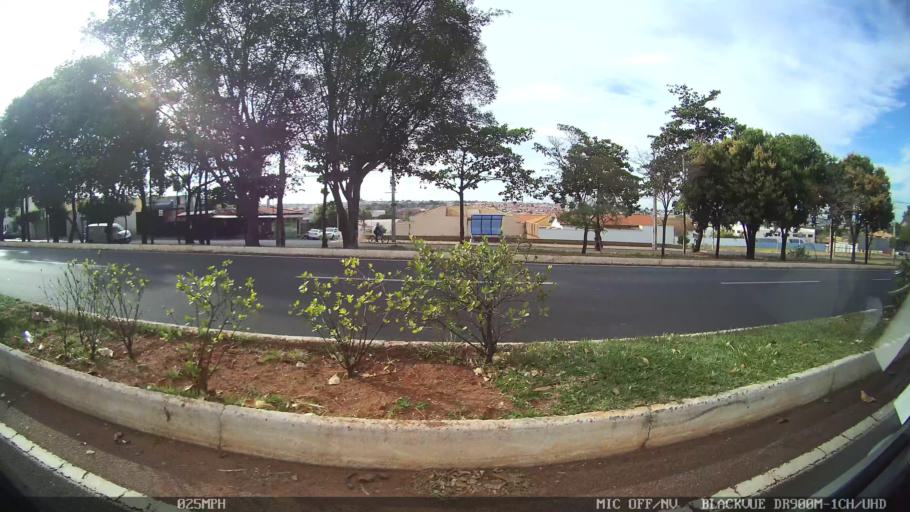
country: BR
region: Sao Paulo
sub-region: Catanduva
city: Catanduva
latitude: -21.1148
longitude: -48.9634
